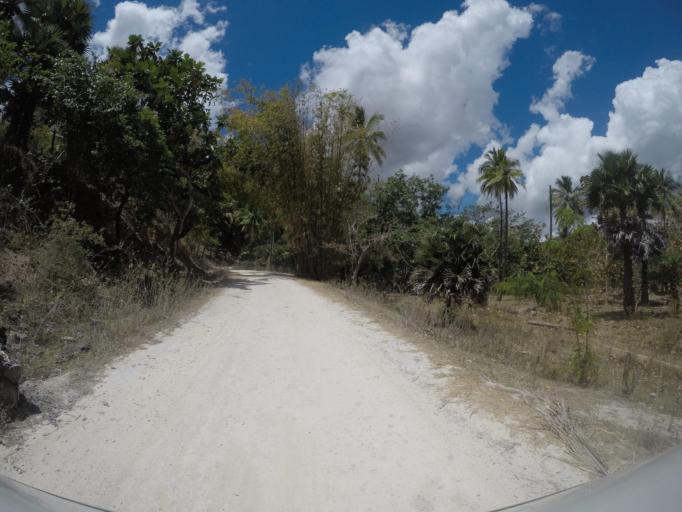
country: TL
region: Baucau
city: Baucau
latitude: -8.4873
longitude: 126.6454
